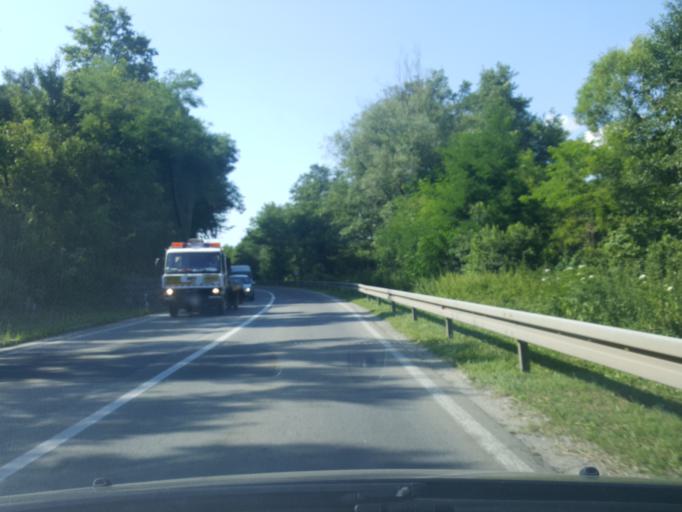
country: RS
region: Central Serbia
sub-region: Moravicki Okrug
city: Gornji Milanovac
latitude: 44.0772
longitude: 20.4860
